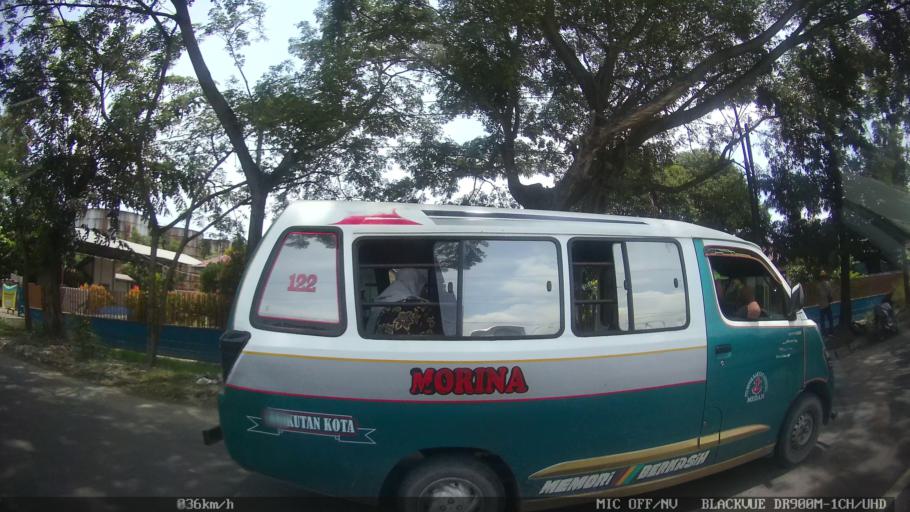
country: ID
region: North Sumatra
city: Labuhan Deli
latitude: 3.7286
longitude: 98.6769
